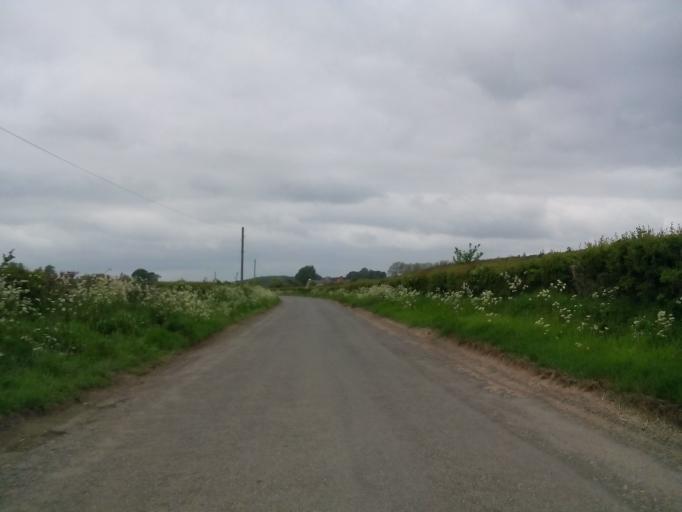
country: GB
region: England
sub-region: Northamptonshire
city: Oundle
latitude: 52.5165
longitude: -0.5131
